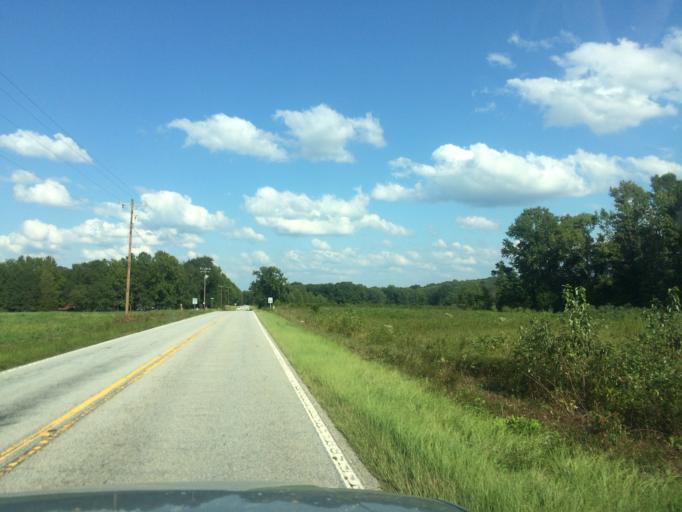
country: US
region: South Carolina
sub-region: Greenwood County
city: Ware Shoals
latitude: 34.4273
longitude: -82.2314
